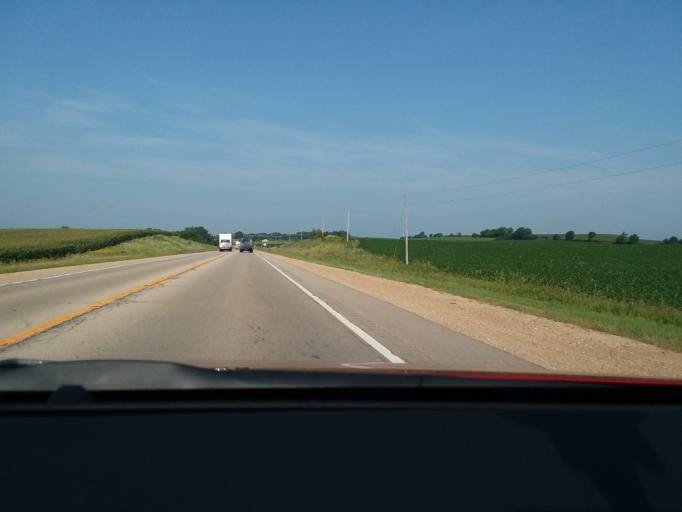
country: US
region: Wisconsin
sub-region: Dane County
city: Windsor
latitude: 43.1957
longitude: -89.3722
